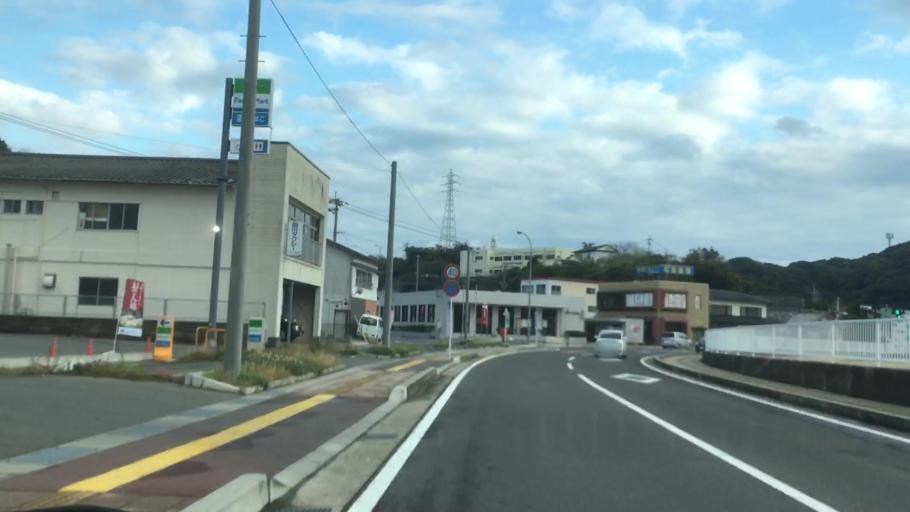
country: JP
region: Nagasaki
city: Togitsu
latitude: 32.9356
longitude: 129.6404
